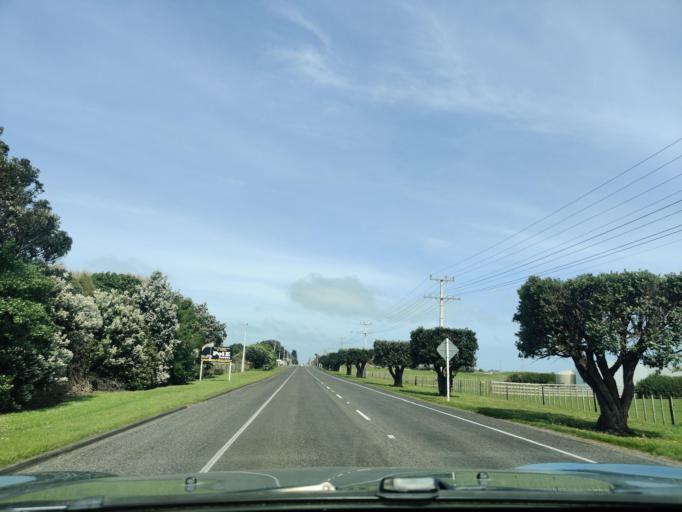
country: NZ
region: Taranaki
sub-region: South Taranaki District
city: Patea
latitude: -39.7447
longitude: 174.4636
